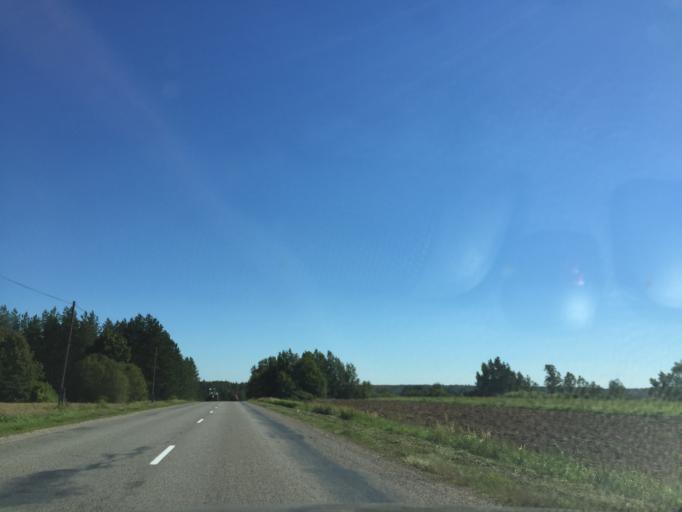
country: LV
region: Akniste
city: Akniste
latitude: 56.1317
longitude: 25.8267
